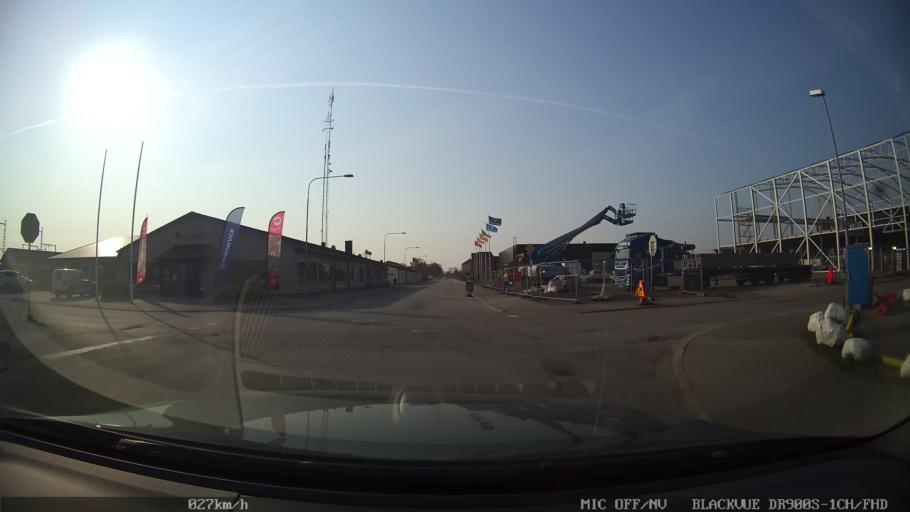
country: SE
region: Skane
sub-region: Ystads Kommun
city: Ystad
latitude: 55.4349
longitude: 13.8335
